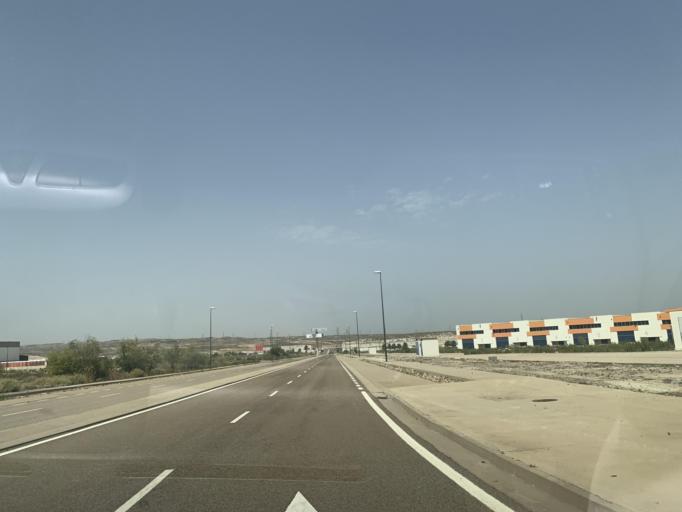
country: ES
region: Aragon
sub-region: Provincia de Zaragoza
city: Zaragoza
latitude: 41.5847
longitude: -0.8327
